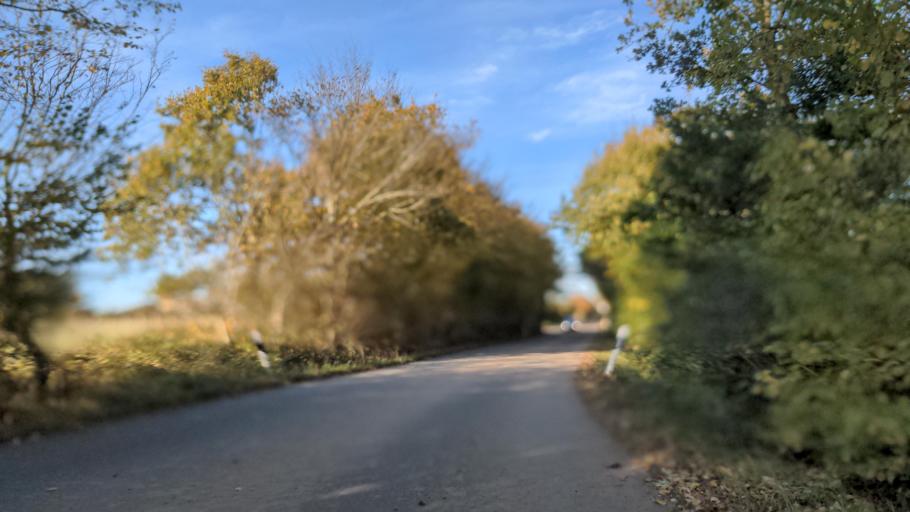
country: DE
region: Schleswig-Holstein
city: Kirchnuchel
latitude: 54.1634
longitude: 10.6688
